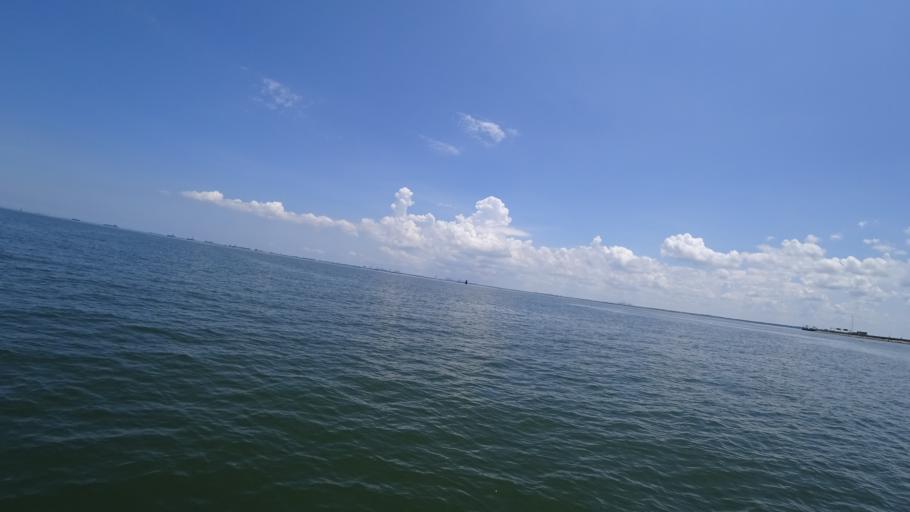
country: US
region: Virginia
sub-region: City of Newport News
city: Newport News
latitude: 36.9524
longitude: -76.4037
